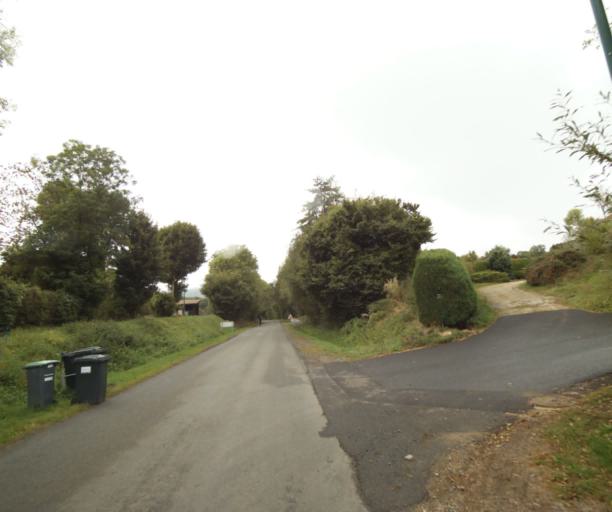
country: FR
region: Auvergne
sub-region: Departement du Puy-de-Dome
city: Saint-Genes-Champanelle
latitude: 45.7281
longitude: 2.9879
